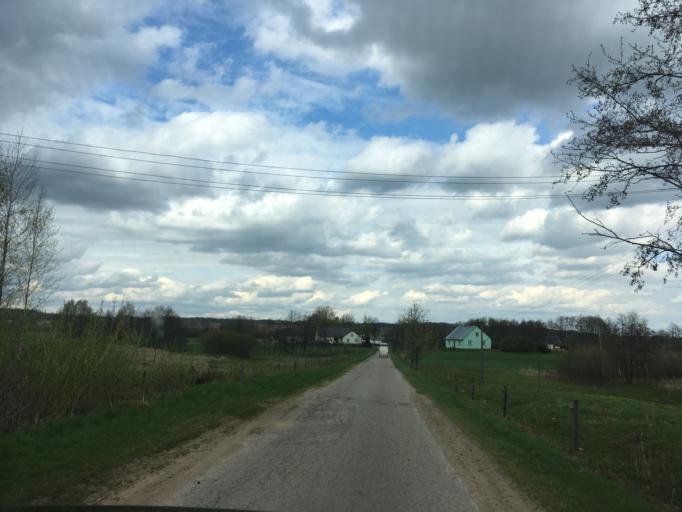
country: PL
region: Podlasie
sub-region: Powiat sejnenski
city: Punsk
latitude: 54.3765
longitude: 22.9483
